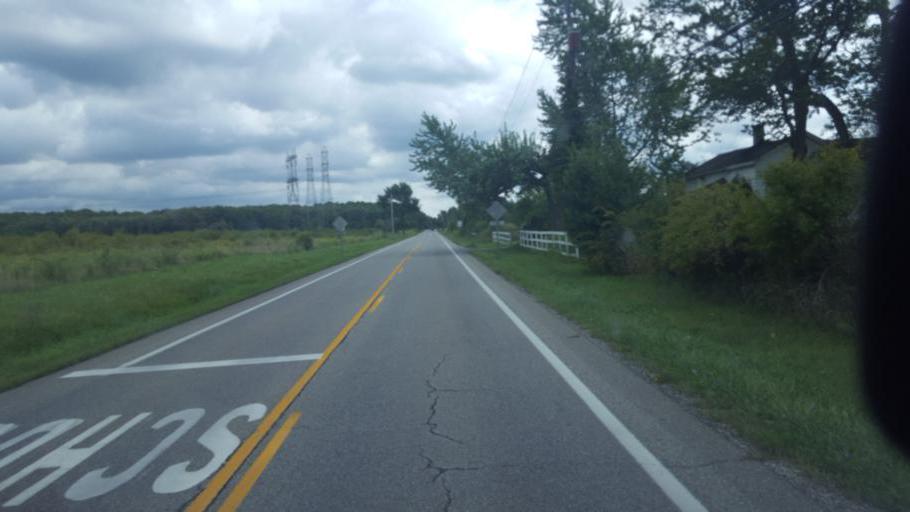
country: US
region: Ohio
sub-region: Geauga County
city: Chardon
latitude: 41.6640
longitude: -81.1459
